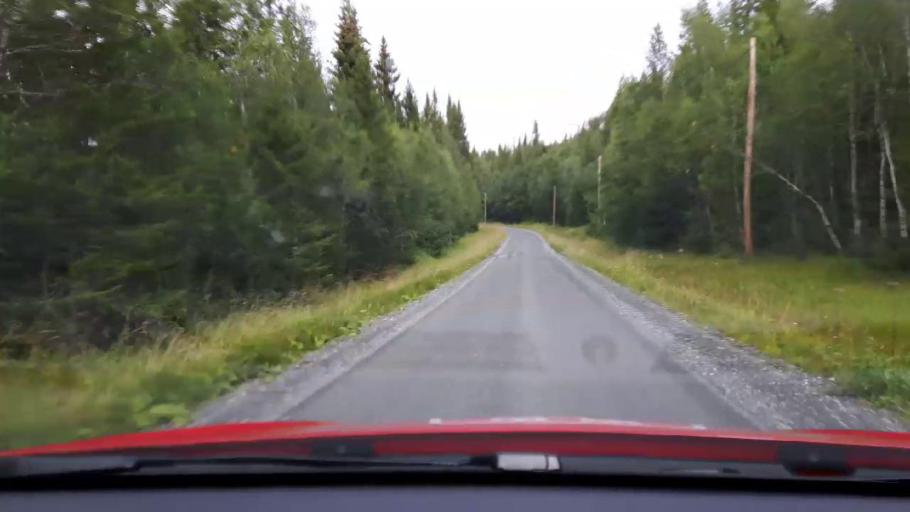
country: SE
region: Jaemtland
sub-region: Are Kommun
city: Are
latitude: 63.7559
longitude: 13.0922
